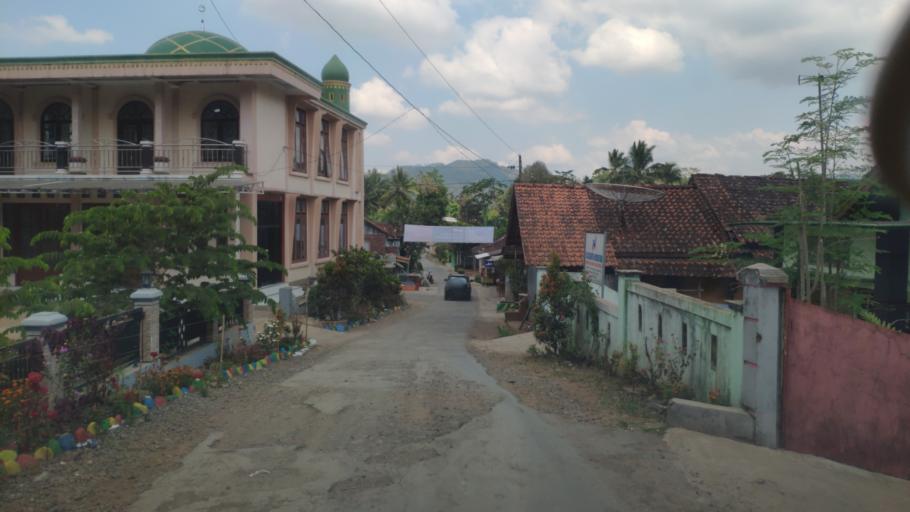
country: ID
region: Central Java
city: Wonosobo
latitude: -7.3219
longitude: 109.6596
